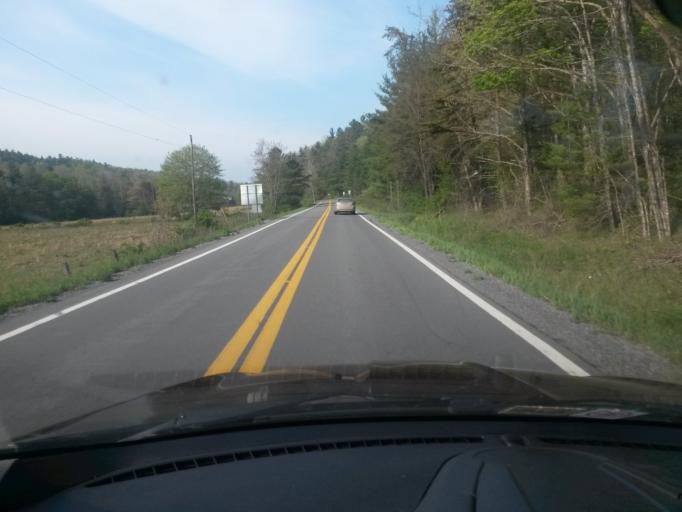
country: US
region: West Virginia
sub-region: Pocahontas County
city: Marlinton
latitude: 38.0617
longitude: -80.0077
